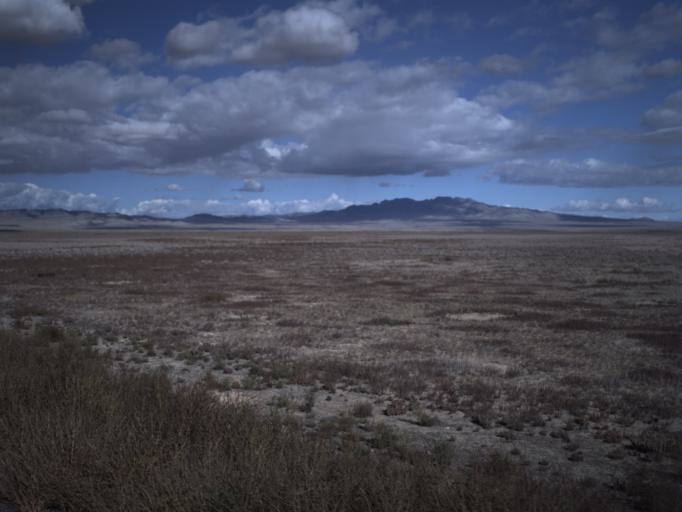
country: US
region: Utah
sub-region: Beaver County
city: Milford
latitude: 38.5211
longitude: -113.6515
